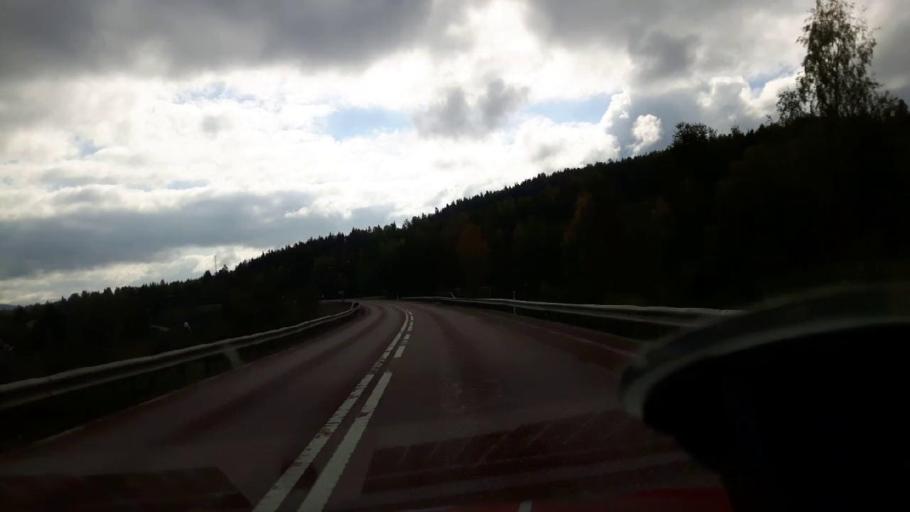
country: SE
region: Gaevleborg
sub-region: Bollnas Kommun
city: Arbra
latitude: 61.5969
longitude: 16.2968
